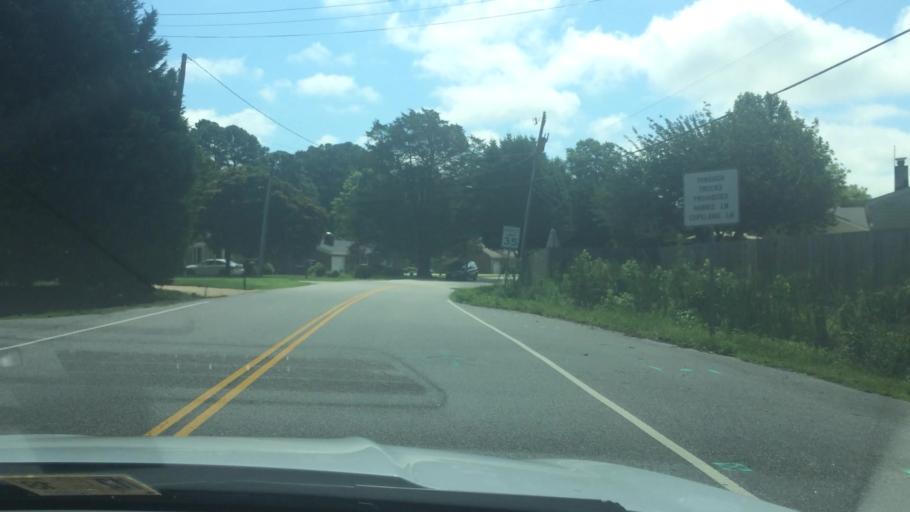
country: US
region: Virginia
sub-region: York County
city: Yorktown
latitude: 37.1955
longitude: -76.4815
